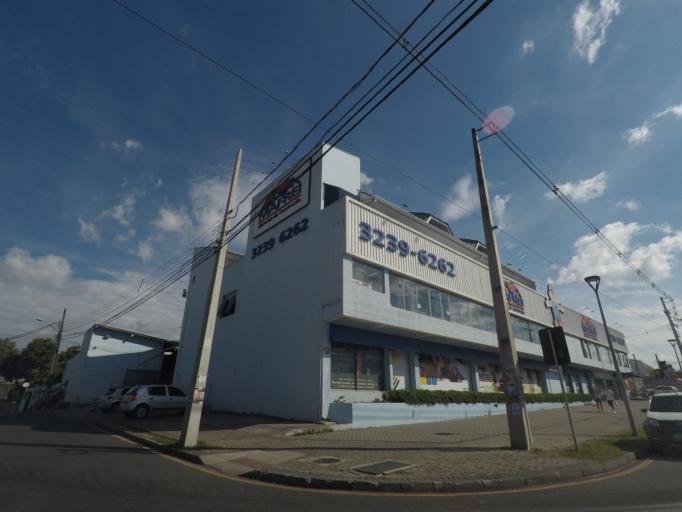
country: BR
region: Parana
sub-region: Curitiba
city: Curitiba
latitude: -25.4775
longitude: -49.3334
